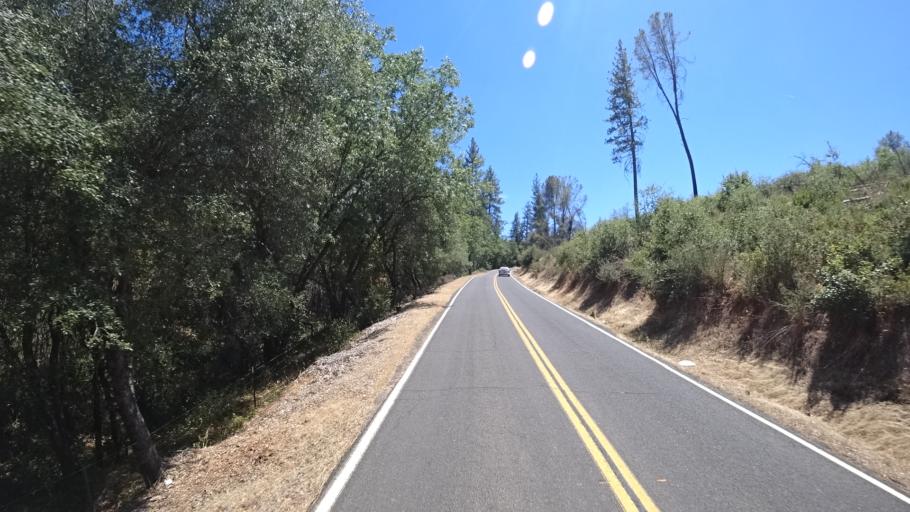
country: US
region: California
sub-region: Calaveras County
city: Forest Meadows
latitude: 38.2151
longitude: -120.4639
